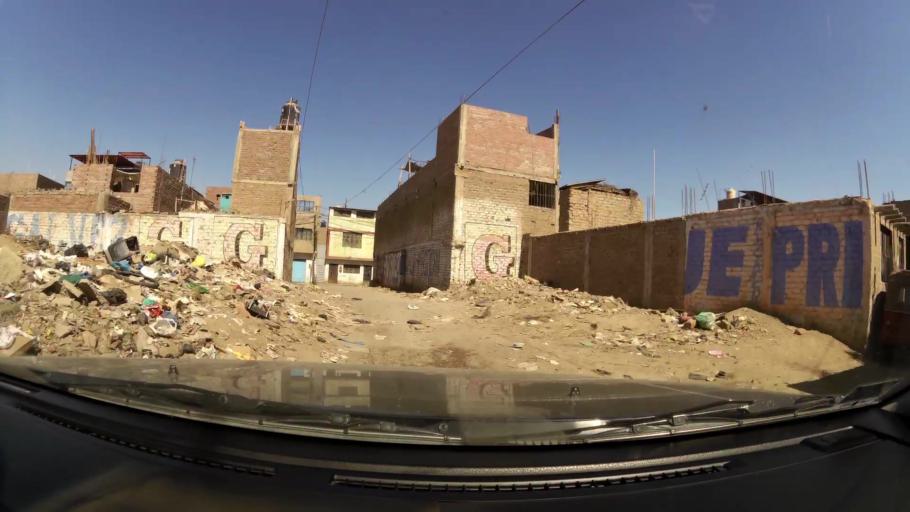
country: PE
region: Ica
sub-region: Provincia de Ica
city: Ica
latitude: -14.0611
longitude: -75.7238
